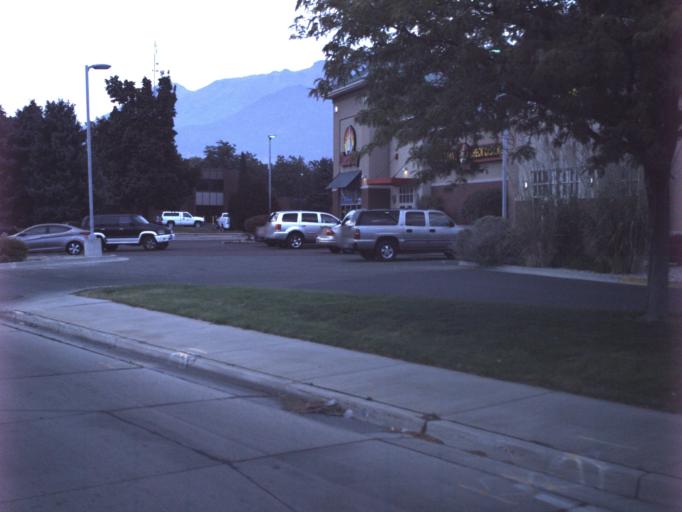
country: US
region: Utah
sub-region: Utah County
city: Orem
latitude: 40.2965
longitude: -111.6946
